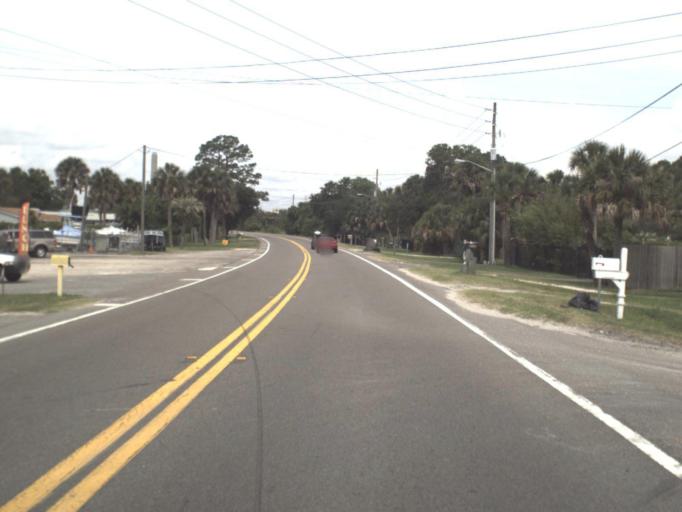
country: US
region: Florida
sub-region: Duval County
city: Jacksonville
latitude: 30.4178
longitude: -81.5326
